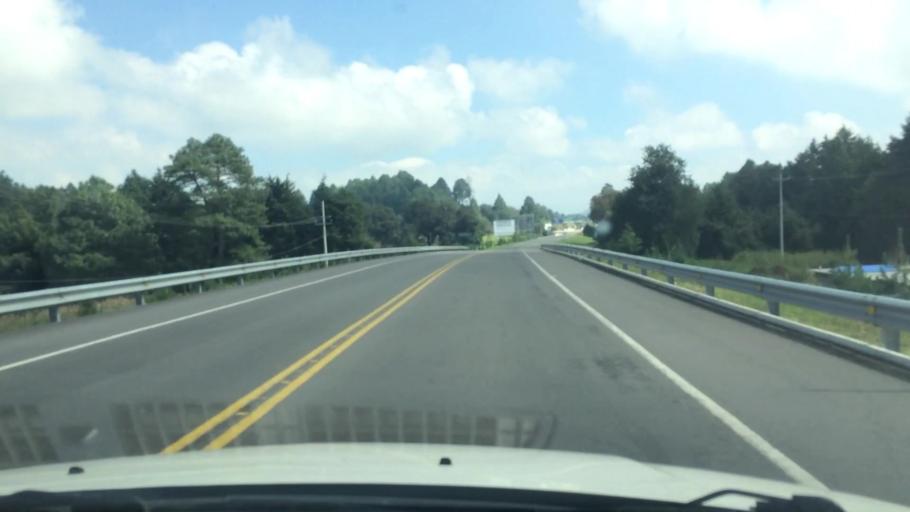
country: MX
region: Mexico
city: Amanalco de Becerra
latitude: 19.3431
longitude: -99.9925
